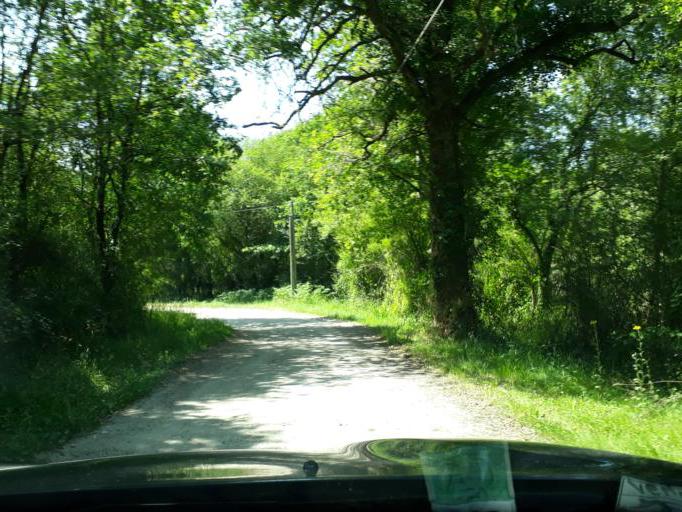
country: FR
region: Centre
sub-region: Departement du Loir-et-Cher
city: Vouzon
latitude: 47.6341
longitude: 2.0499
